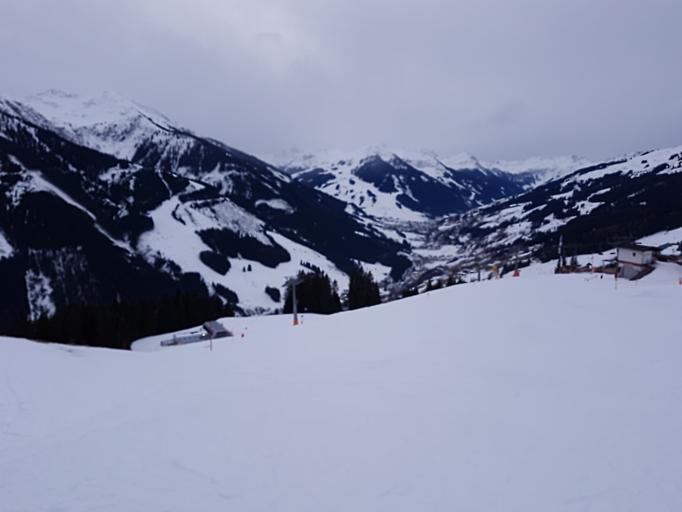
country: AT
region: Salzburg
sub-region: Politischer Bezirk Zell am See
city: Saalbach
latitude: 47.4006
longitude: 12.6511
